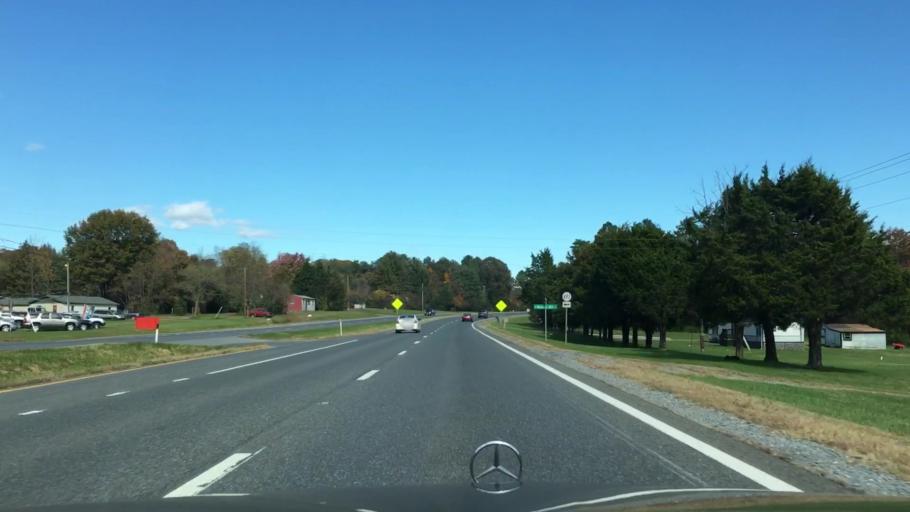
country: US
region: Virginia
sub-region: Campbell County
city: Rustburg
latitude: 37.2082
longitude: -79.2018
